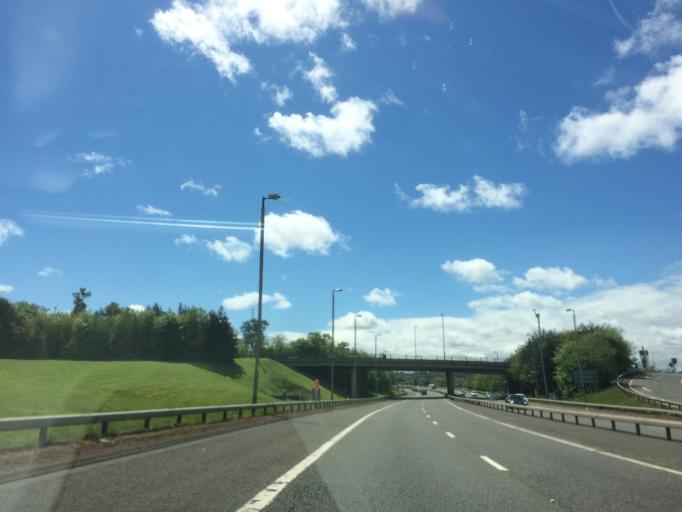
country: GB
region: Scotland
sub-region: East Renfrewshire
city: Giffnock
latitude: 55.8244
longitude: -4.3341
